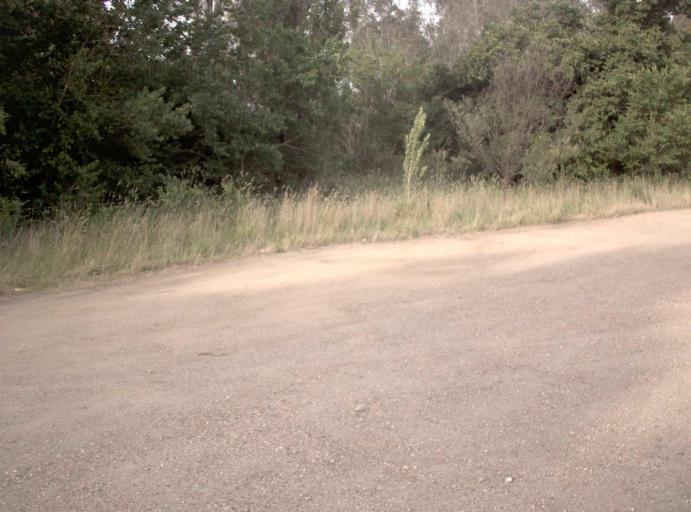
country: AU
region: Victoria
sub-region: Wellington
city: Sale
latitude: -37.9653
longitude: 146.9654
